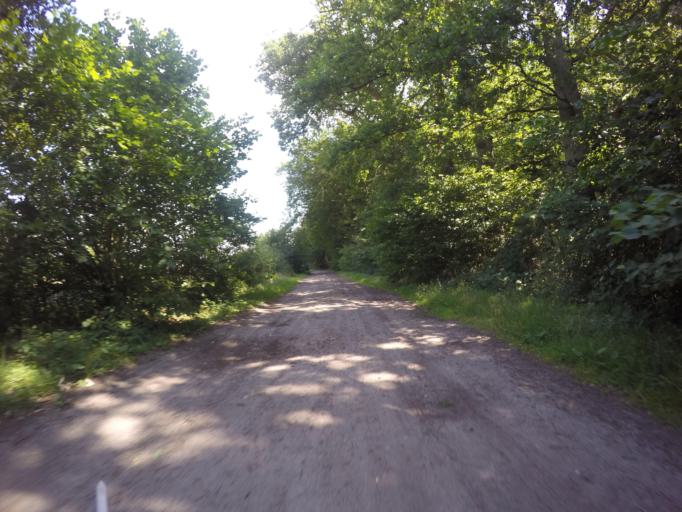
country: DE
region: Lower Saxony
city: Bleckede
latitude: 53.2701
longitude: 10.7072
